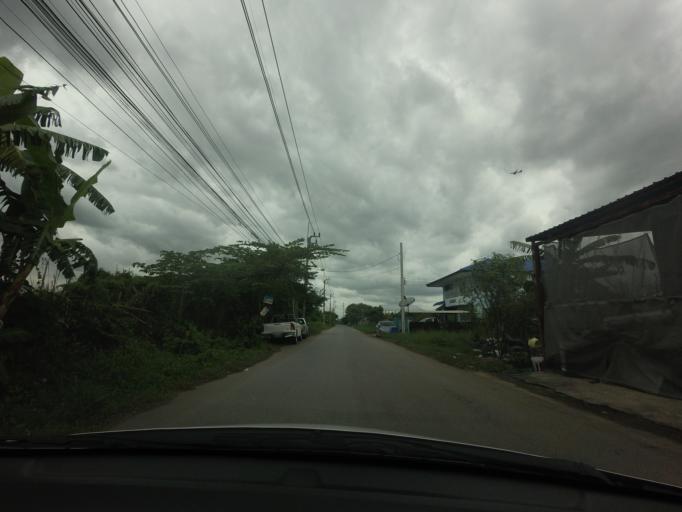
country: TH
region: Bangkok
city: Lat Krabang
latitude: 13.7755
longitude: 100.7711
